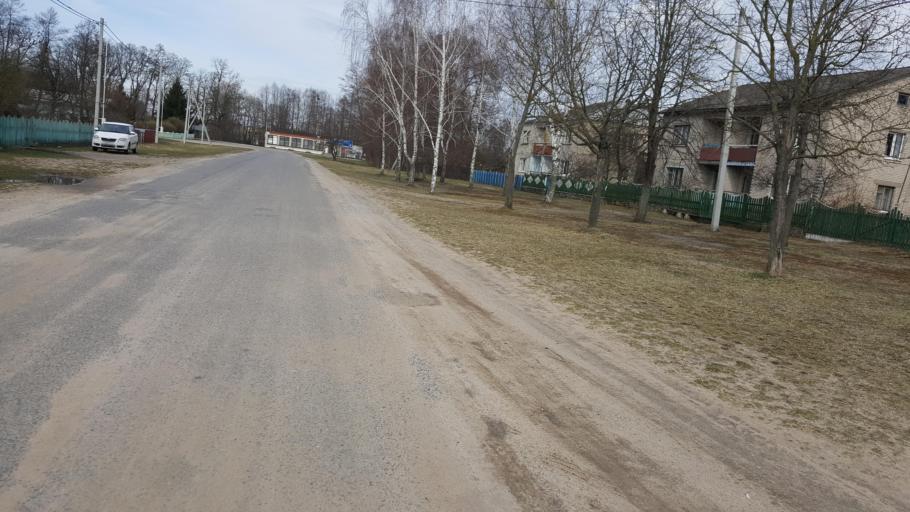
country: BY
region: Brest
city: Kamyanyets
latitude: 52.3924
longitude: 24.0019
